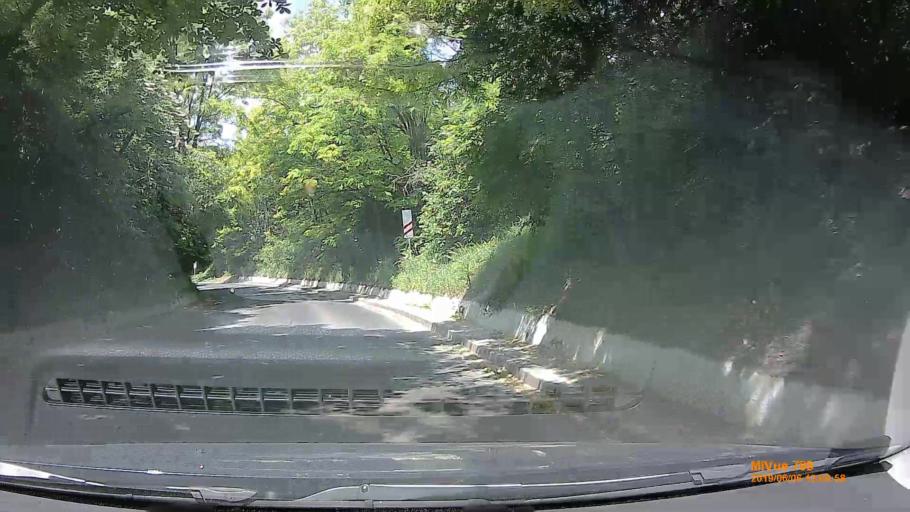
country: HU
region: Pest
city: Kerepes
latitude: 47.5645
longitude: 19.2751
